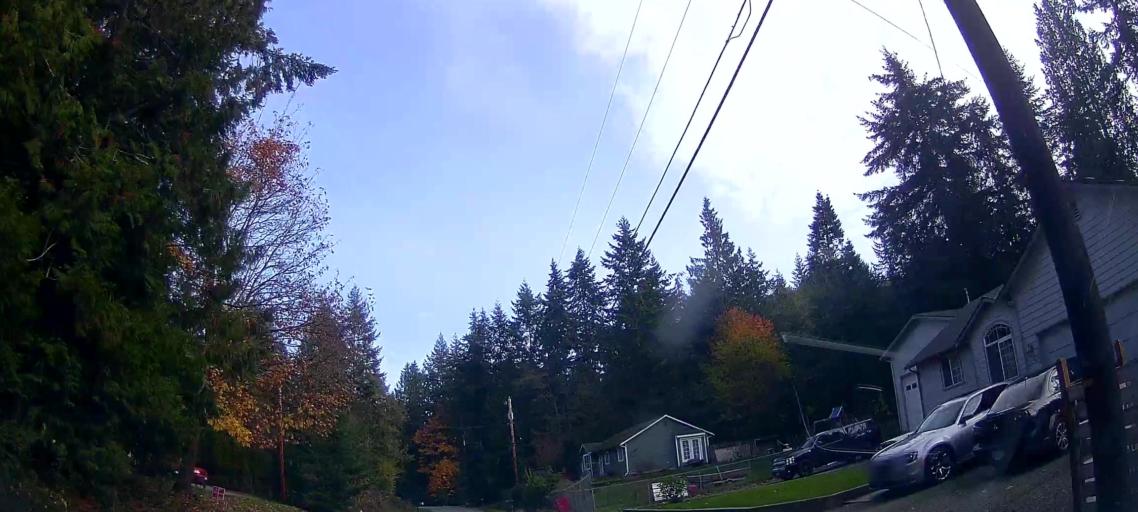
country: US
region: Washington
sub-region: Snohomish County
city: Stanwood
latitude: 48.2797
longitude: -122.3437
